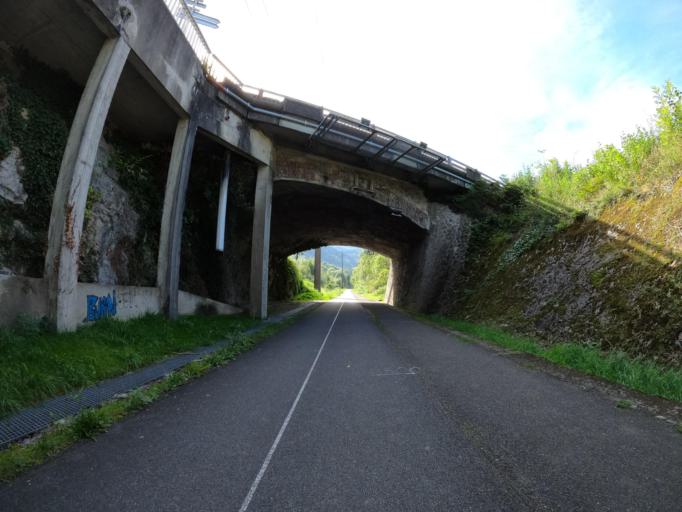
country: FR
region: Midi-Pyrenees
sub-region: Departement des Hautes-Pyrenees
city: Lourdes
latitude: 43.0689
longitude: -0.0407
